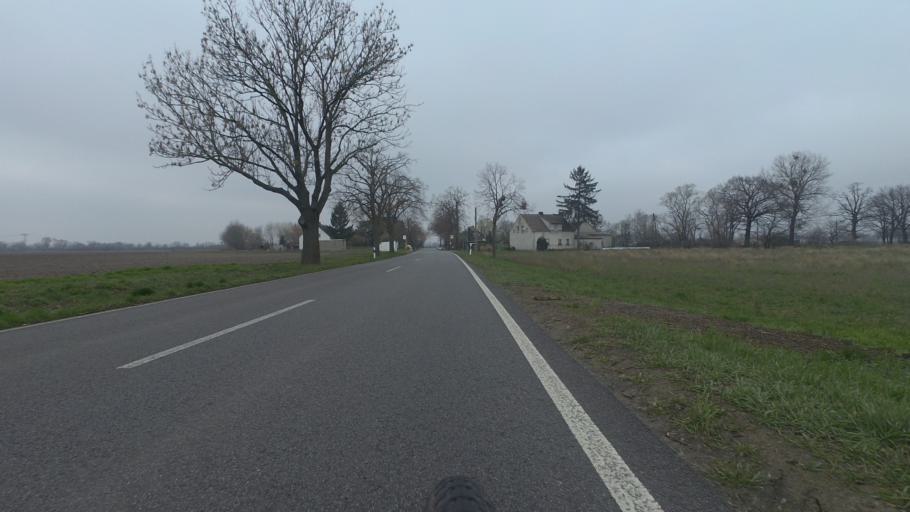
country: DE
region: Brandenburg
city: Nauen
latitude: 52.6303
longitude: 12.8528
